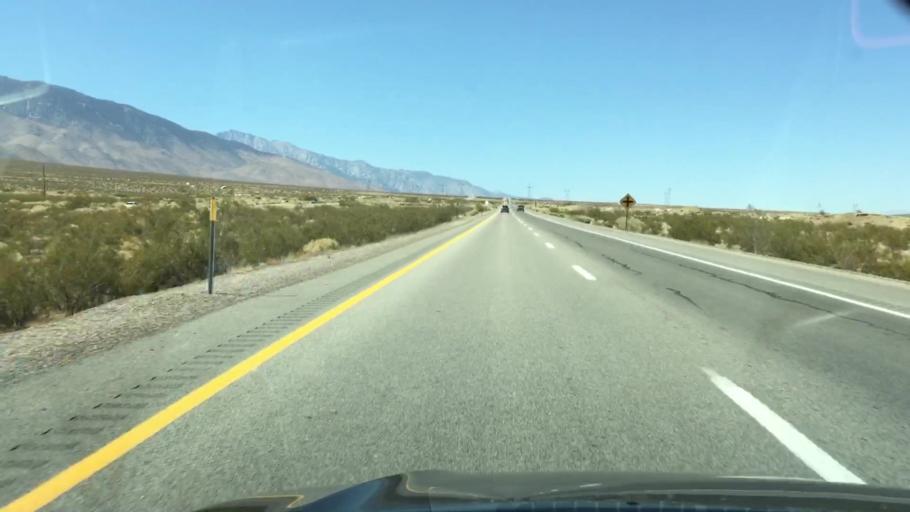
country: US
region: California
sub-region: Kern County
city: Inyokern
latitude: 36.0911
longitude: -117.9620
